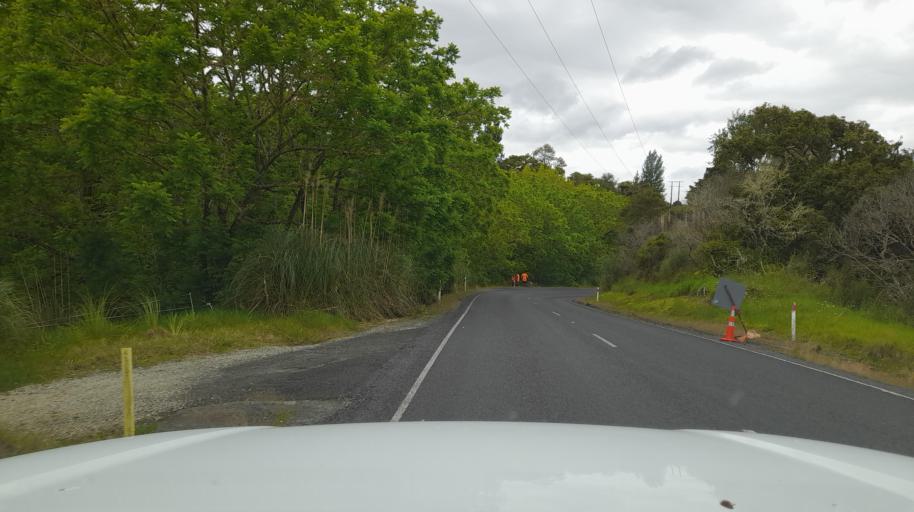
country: NZ
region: Northland
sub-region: Far North District
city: Taipa
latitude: -35.2626
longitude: 173.5253
